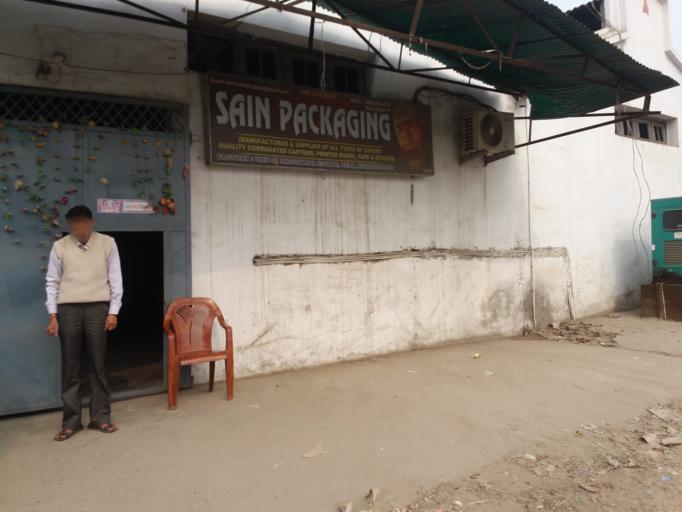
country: IN
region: Bihar
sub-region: Muzaffarpur
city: Muzaffarpur
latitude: 26.0997
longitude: 85.4057
